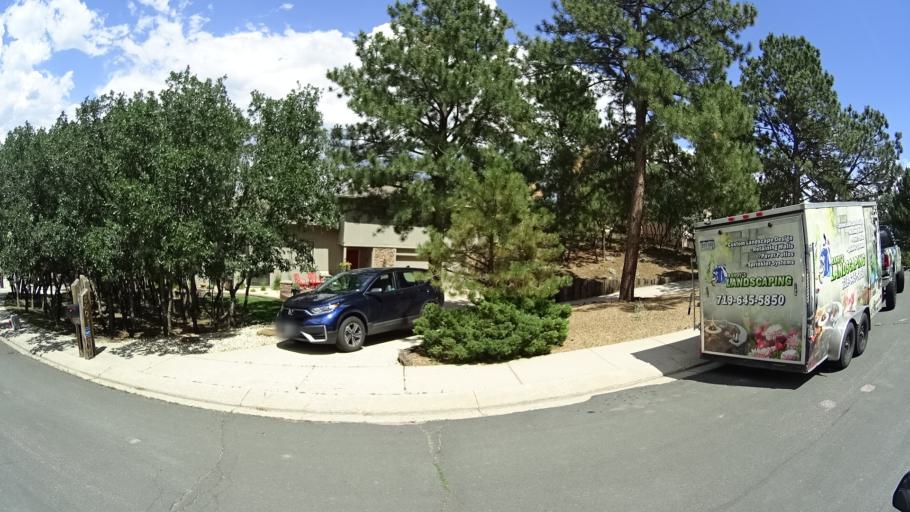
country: US
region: Colorado
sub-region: El Paso County
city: Air Force Academy
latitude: 38.9354
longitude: -104.8409
